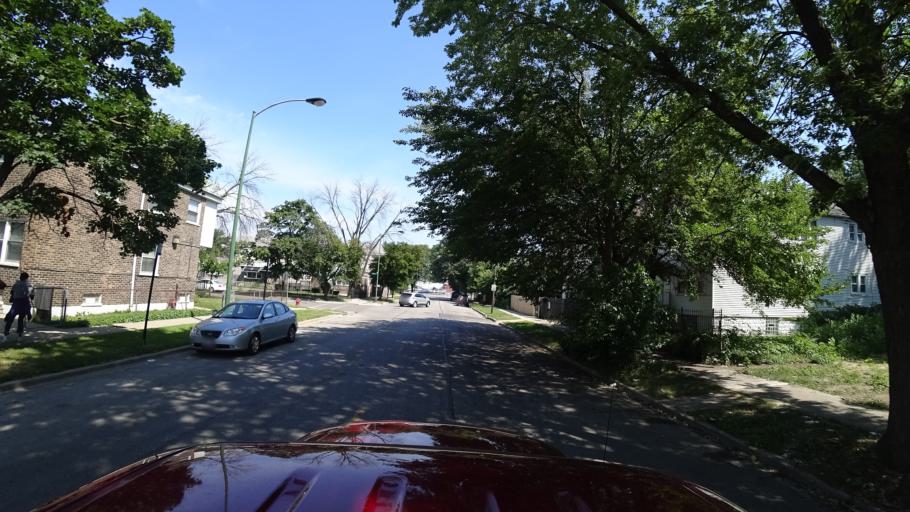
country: US
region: Illinois
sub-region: Cook County
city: Chicago
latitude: 41.8178
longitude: -87.6336
